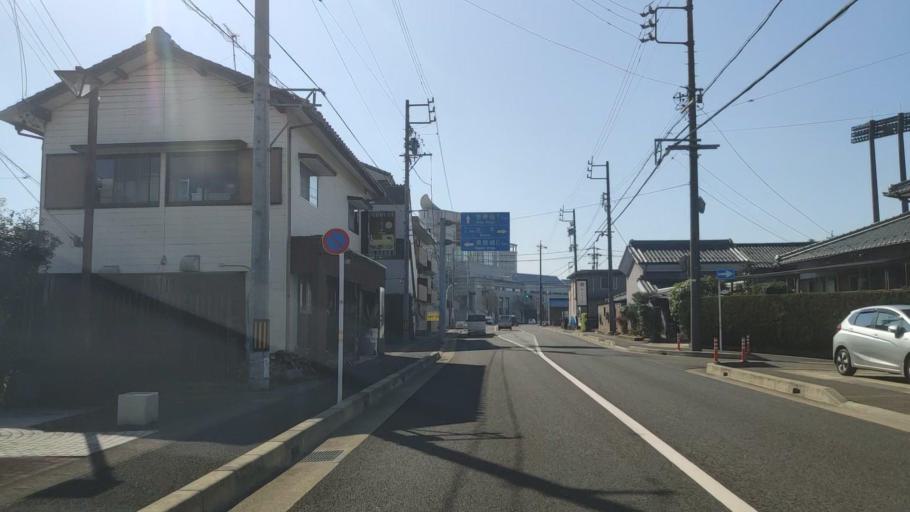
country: JP
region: Gifu
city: Gifu-shi
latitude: 35.4436
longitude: 136.7685
